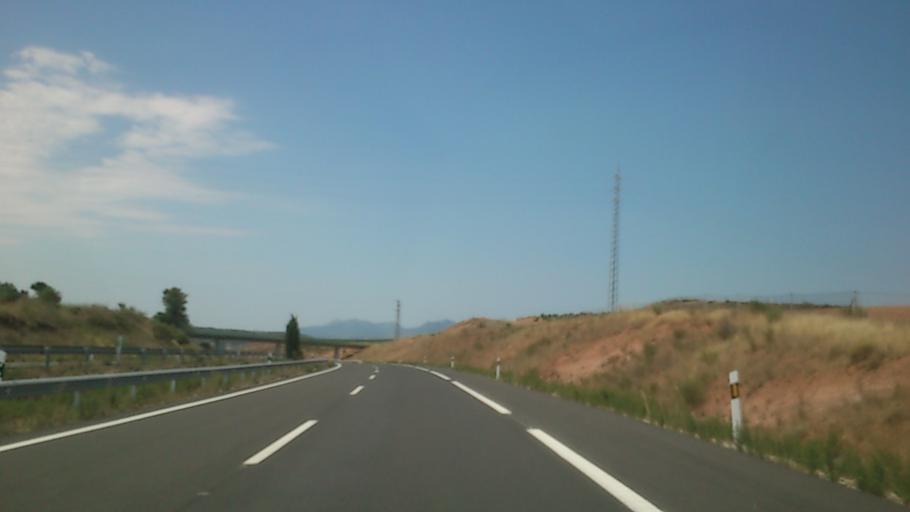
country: ES
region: La Rioja
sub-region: Provincia de La Rioja
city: Fuenmayor
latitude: 42.4540
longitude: -2.5755
